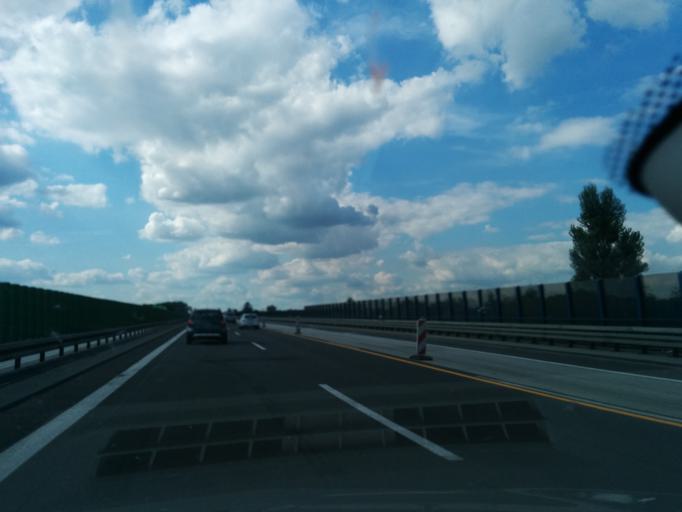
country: DE
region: Brandenburg
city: Woltersdorf
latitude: 52.4709
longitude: 13.7738
